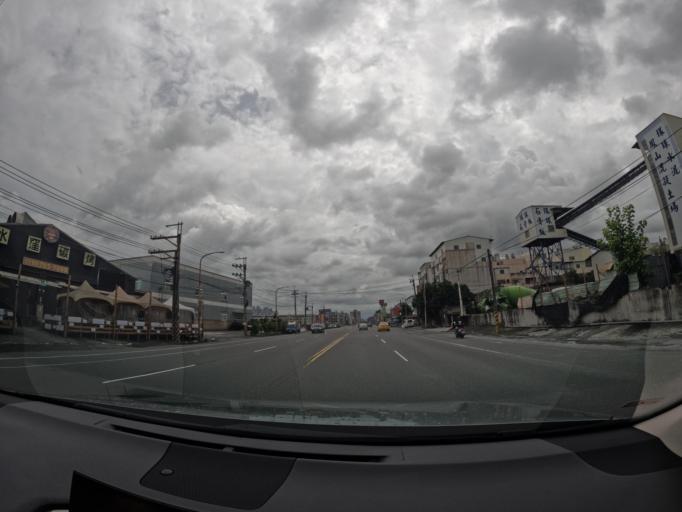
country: TW
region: Taiwan
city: Fengshan
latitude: 22.6320
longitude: 120.3863
